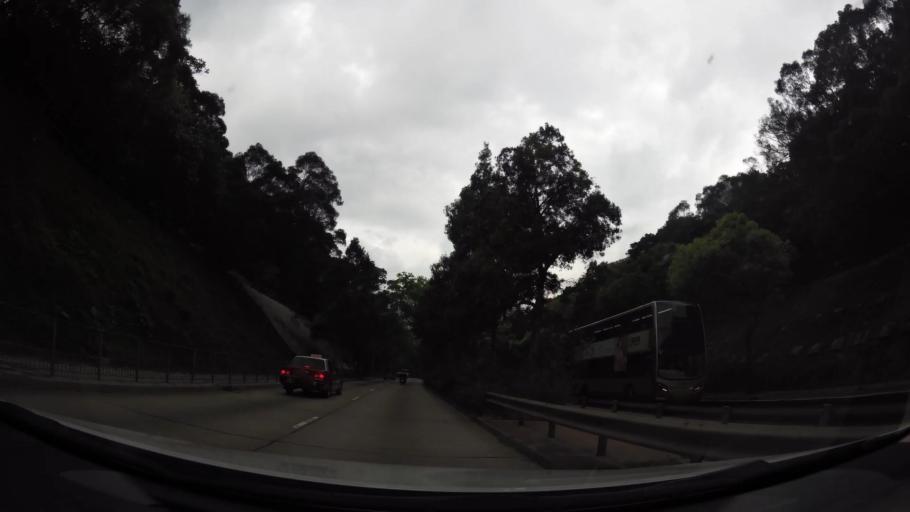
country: HK
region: Kowloon City
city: Kowloon
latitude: 22.3332
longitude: 114.2205
